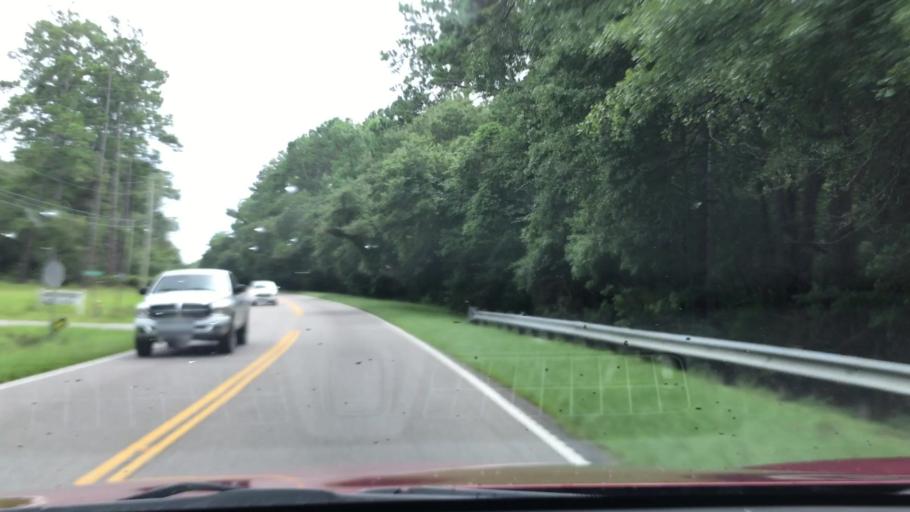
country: US
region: South Carolina
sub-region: Georgetown County
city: Georgetown
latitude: 33.4755
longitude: -79.2785
